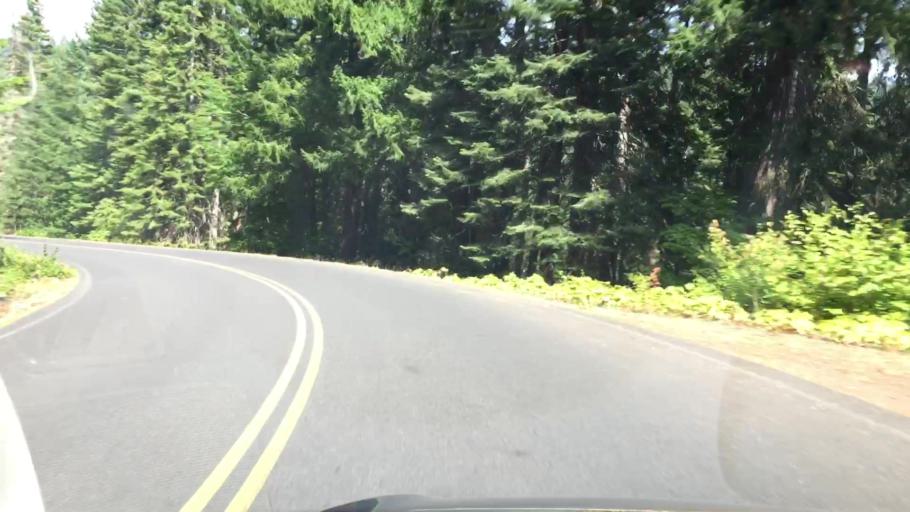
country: US
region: Washington
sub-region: Klickitat County
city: White Salmon
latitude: 46.0494
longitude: -121.5551
